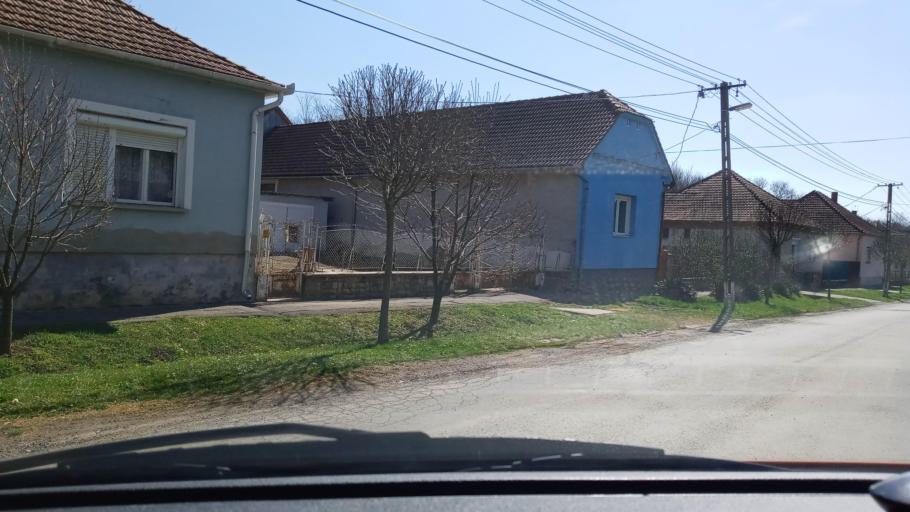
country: HU
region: Baranya
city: Pecsvarad
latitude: 46.0679
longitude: 18.4488
